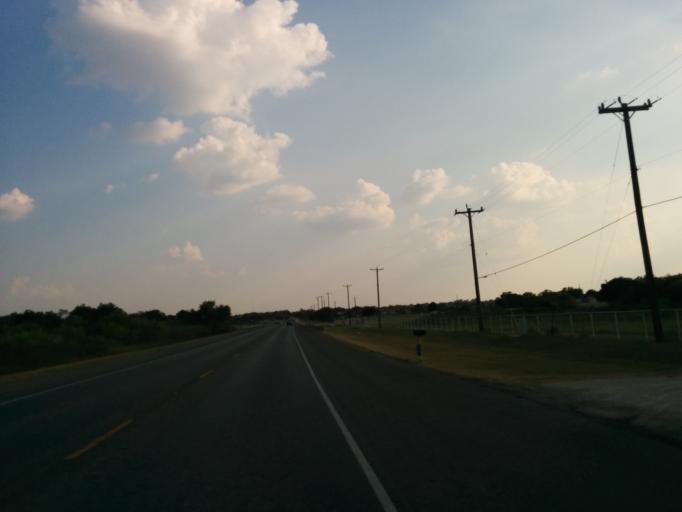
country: US
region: Texas
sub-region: Bexar County
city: Saint Hedwig
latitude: 29.3854
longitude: -98.2394
